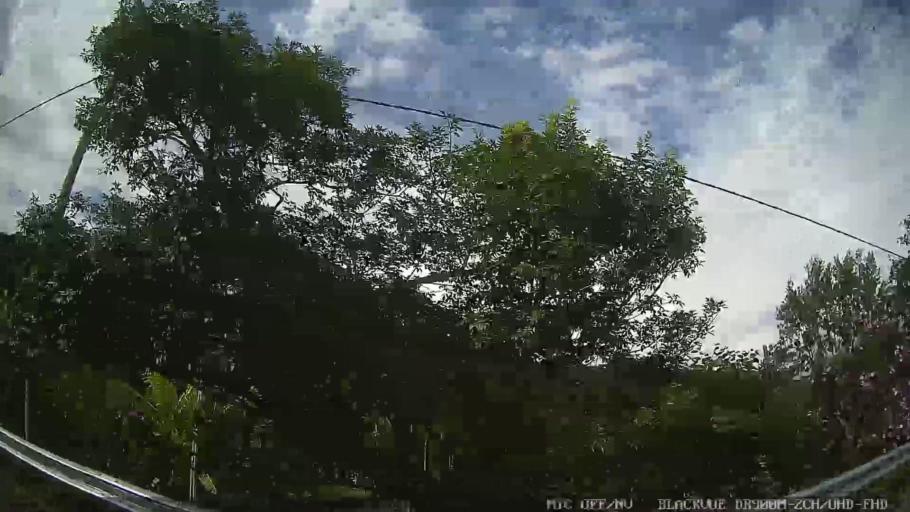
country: BR
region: Sao Paulo
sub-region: Biritiba-Mirim
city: Biritiba Mirim
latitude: -23.5414
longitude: -45.9293
